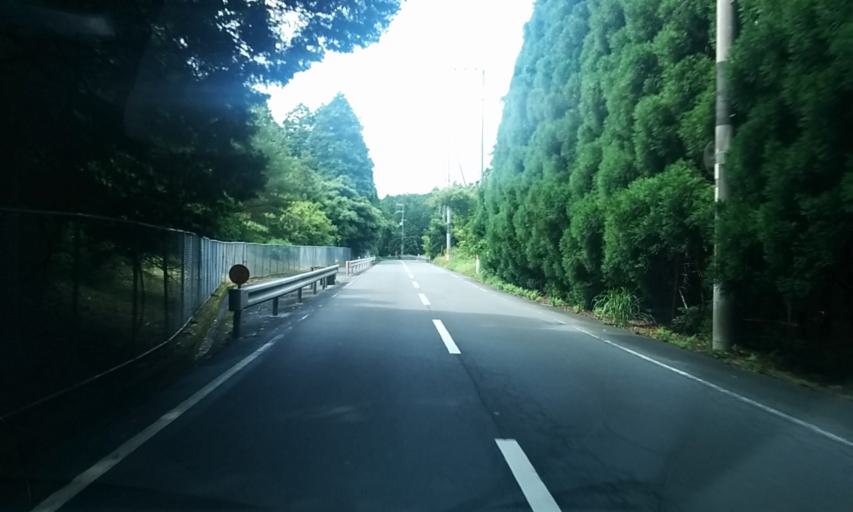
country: JP
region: Kyoto
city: Kameoka
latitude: 34.9982
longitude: 135.4785
